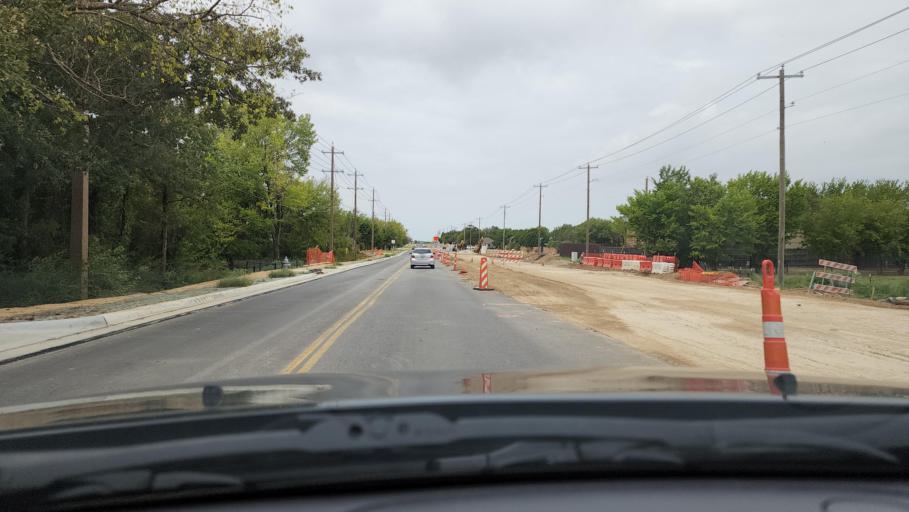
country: US
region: Texas
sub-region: Denton County
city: Corinth
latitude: 33.1469
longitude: -97.1089
